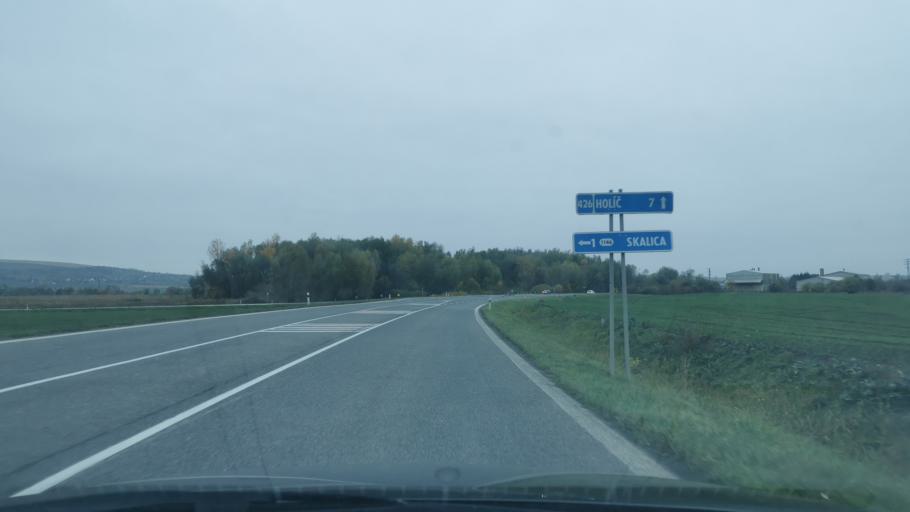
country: SK
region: Trnavsky
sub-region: Okres Skalica
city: Skalica
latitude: 48.8377
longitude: 17.2084
